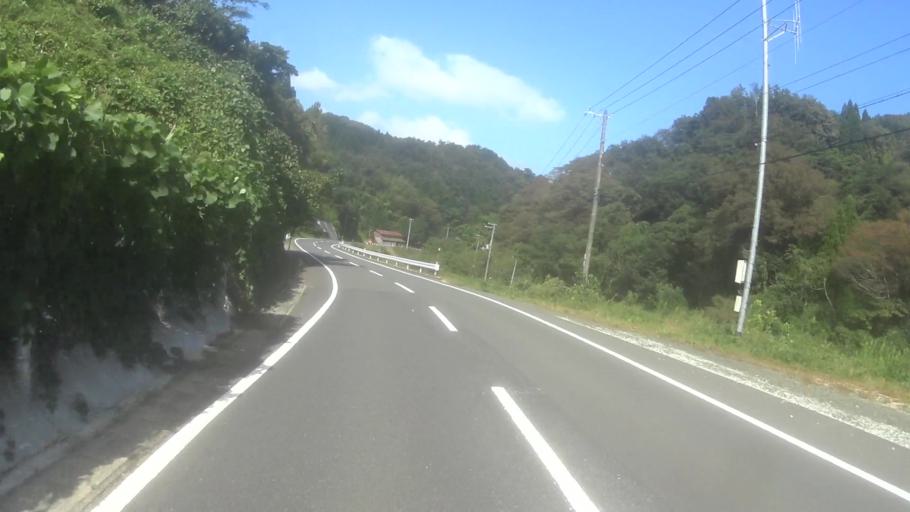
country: JP
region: Kyoto
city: Miyazu
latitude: 35.6292
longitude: 135.1251
